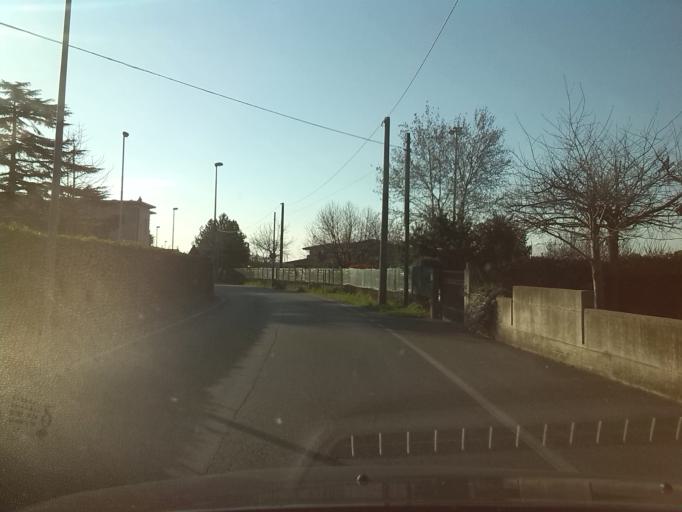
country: IT
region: Friuli Venezia Giulia
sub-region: Provincia di Gorizia
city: Cormons
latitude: 45.9602
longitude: 13.4596
